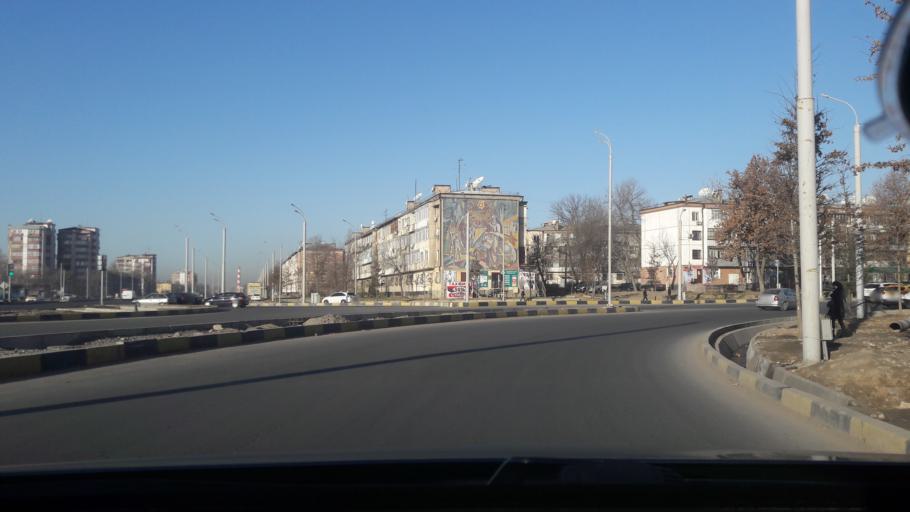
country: TJ
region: Dushanbe
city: Dushanbe
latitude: 38.5587
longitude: 68.7556
